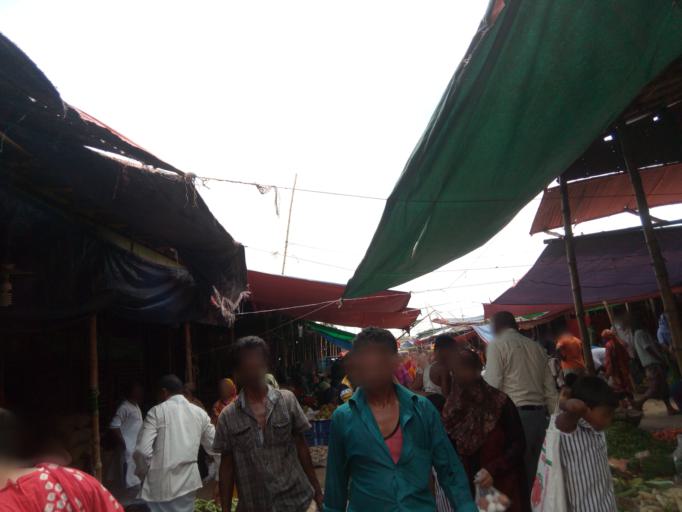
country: BD
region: Dhaka
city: Azimpur
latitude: 23.7474
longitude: 90.3600
